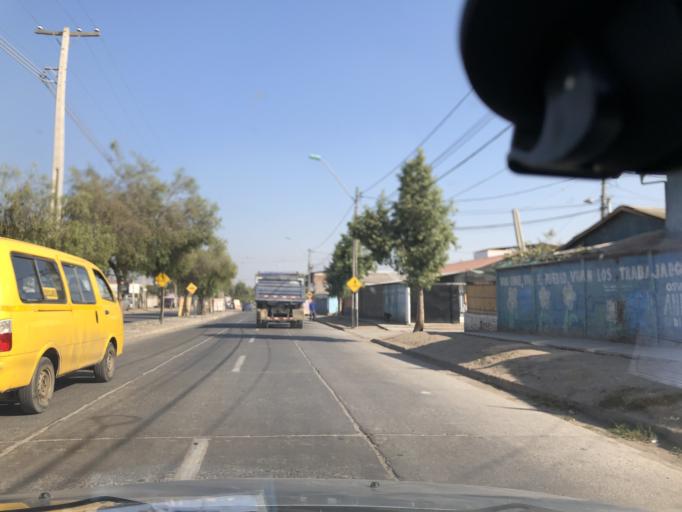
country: CL
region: Santiago Metropolitan
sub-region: Provincia de Cordillera
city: Puente Alto
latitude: -33.6188
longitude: -70.5919
